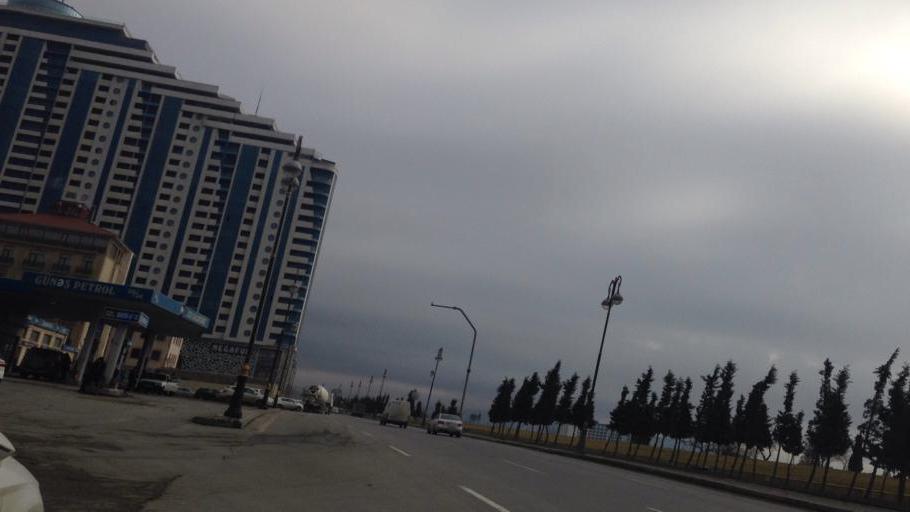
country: AZ
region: Baki
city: Baku
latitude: 40.3772
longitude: 49.8712
